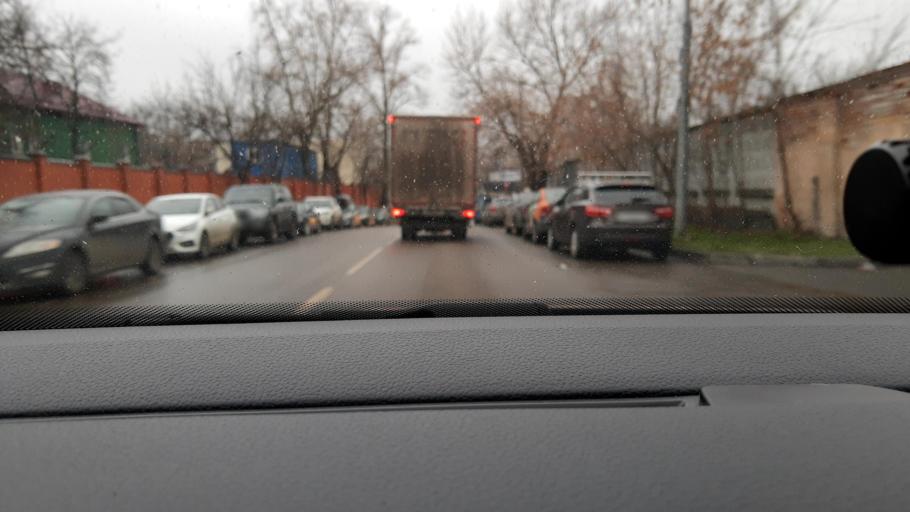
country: RU
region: Moscow
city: Ryazanskiy
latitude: 55.7218
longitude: 37.7638
